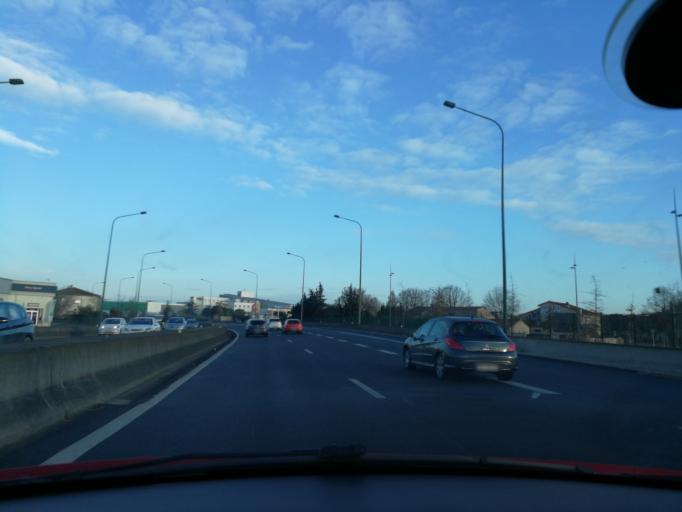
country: FR
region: Midi-Pyrenees
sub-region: Departement de la Haute-Garonne
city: Blagnac
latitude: 43.6401
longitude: 1.3755
